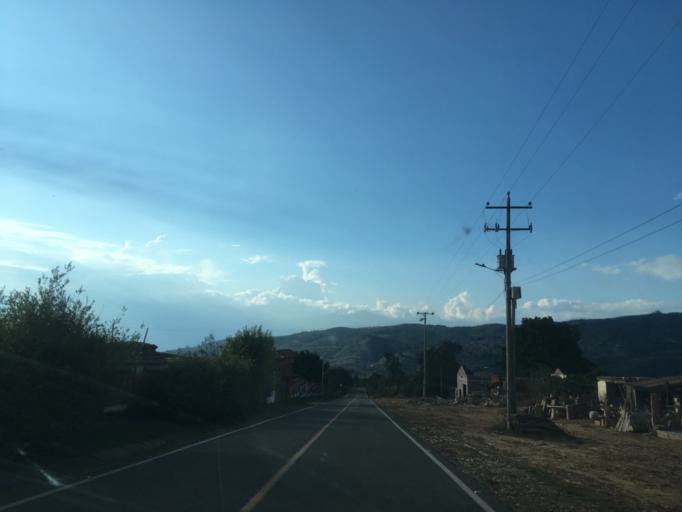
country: CO
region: Santander
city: Villanueva
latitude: 6.6388
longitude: -73.1851
